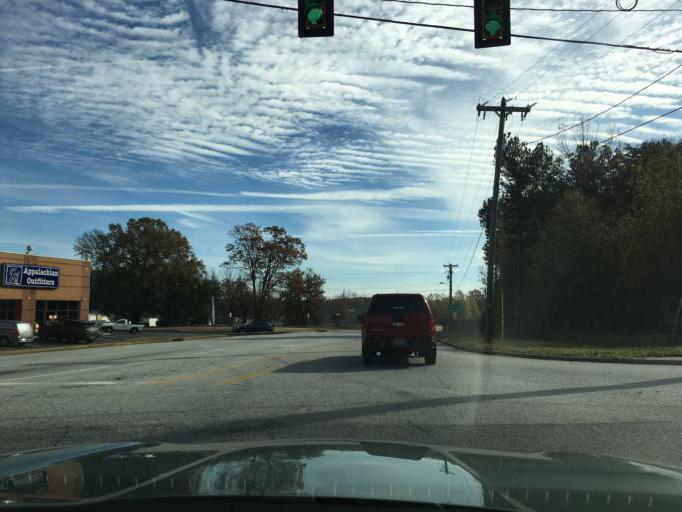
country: US
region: South Carolina
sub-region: Greenville County
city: Wade Hampton
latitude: 34.8423
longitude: -82.3298
